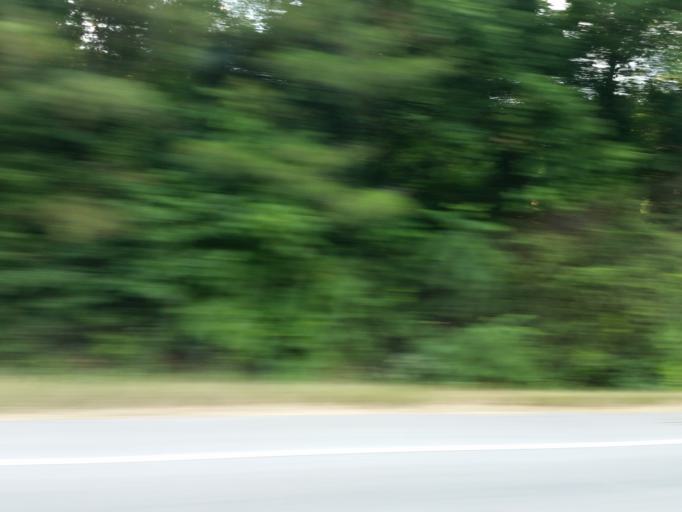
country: US
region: Tennessee
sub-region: Maury County
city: Mount Pleasant
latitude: 35.5810
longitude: -87.3188
